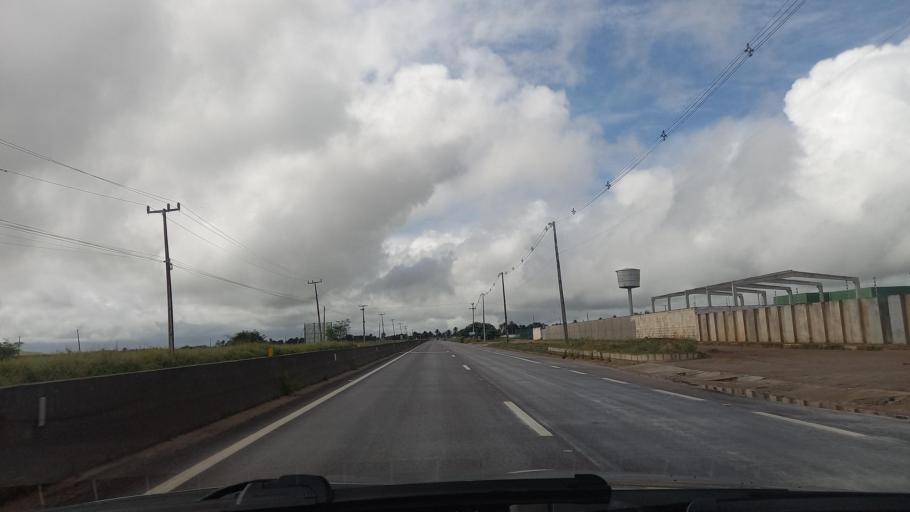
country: BR
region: Alagoas
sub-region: Limoeiro De Anadia
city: Limoeiro de Anadia
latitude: -9.7619
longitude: -36.5405
